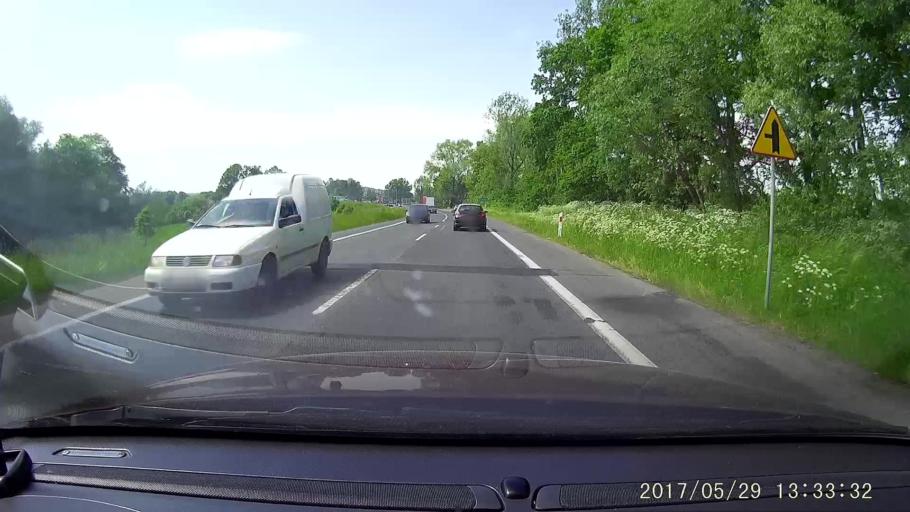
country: PL
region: Lower Silesian Voivodeship
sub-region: Powiat lubanski
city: Luban
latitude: 51.0978
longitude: 15.3125
